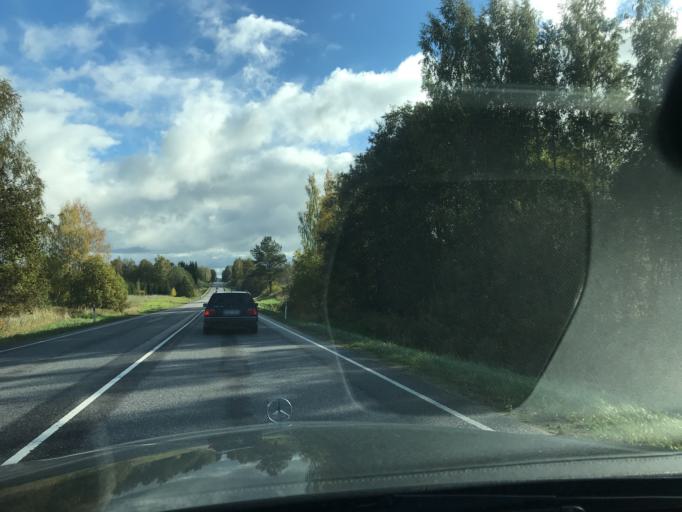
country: EE
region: Vorumaa
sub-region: Voru linn
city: Voru
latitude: 57.7805
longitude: 27.1109
